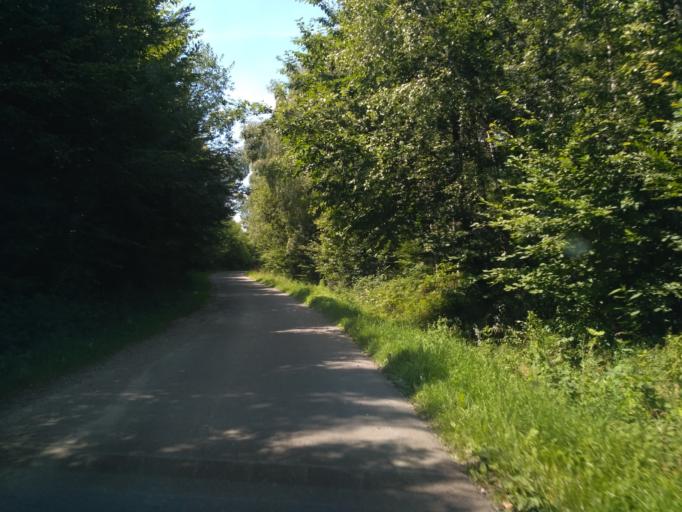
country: PL
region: Subcarpathian Voivodeship
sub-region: Powiat strzyzowski
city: Jawornik
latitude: 49.8582
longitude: 21.8863
